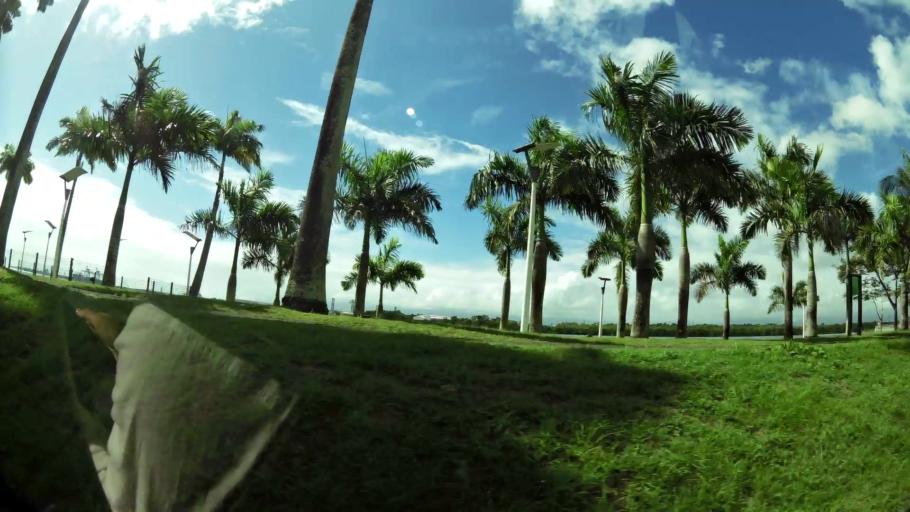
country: GP
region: Guadeloupe
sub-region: Guadeloupe
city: Pointe-a-Pitre
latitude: 16.2477
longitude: -61.5452
